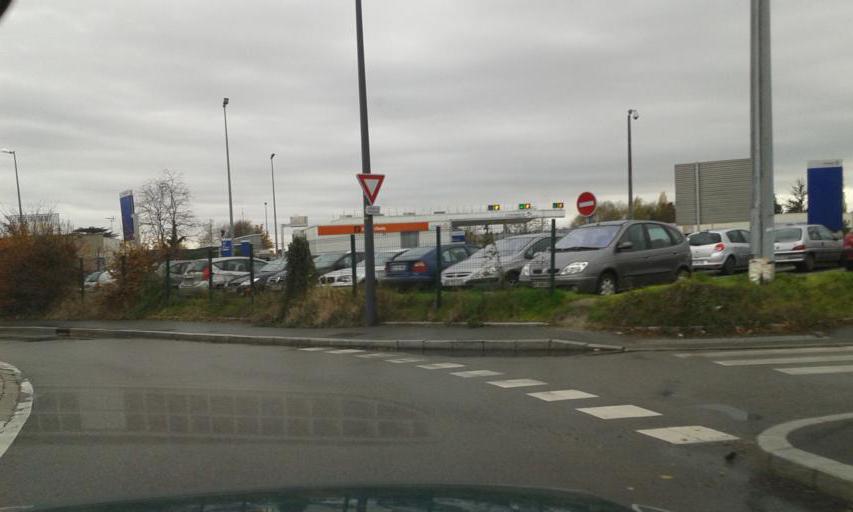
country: FR
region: Centre
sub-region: Departement du Loiret
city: Saint-Jean-de-la-Ruelle
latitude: 47.8986
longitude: 1.8547
